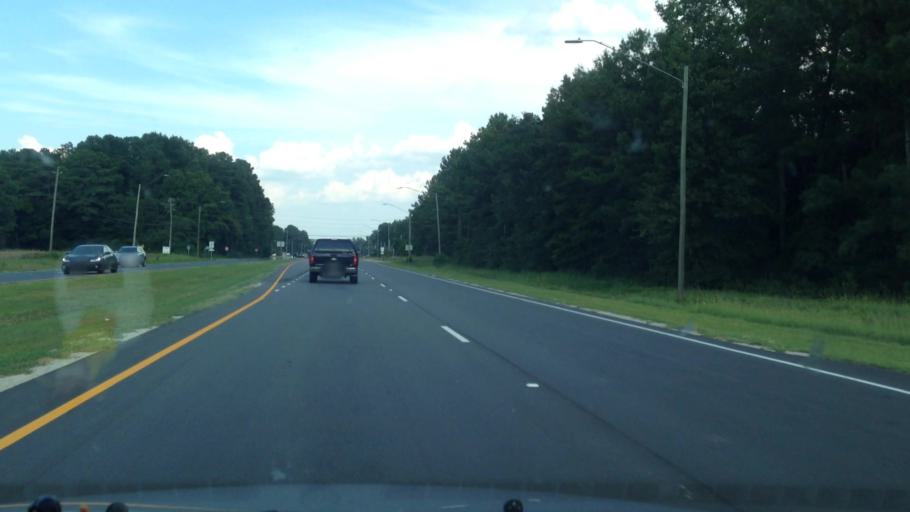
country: US
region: North Carolina
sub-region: Harnett County
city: Lillington
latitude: 35.4095
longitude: -78.7771
